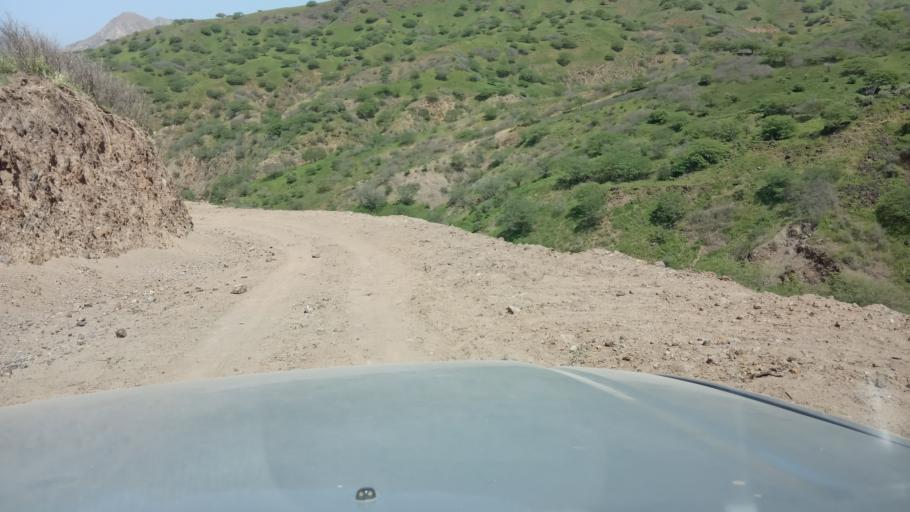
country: CV
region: Santa Catarina
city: Assomada
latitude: 15.1128
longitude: -23.7277
